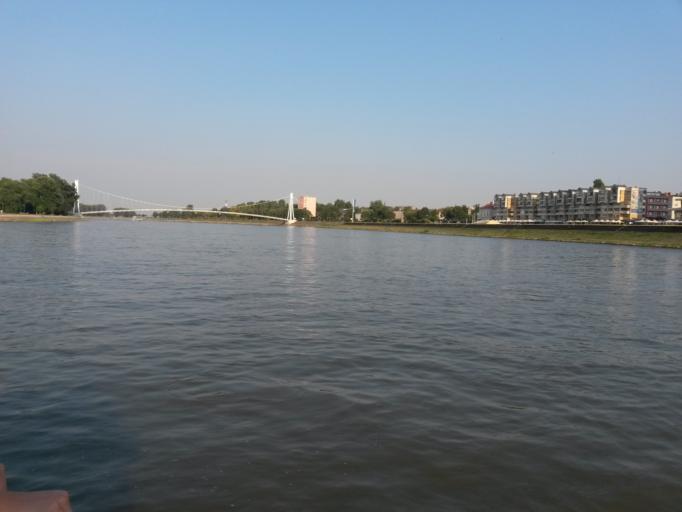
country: HR
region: Osjecko-Baranjska
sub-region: Grad Osijek
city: Osijek
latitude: 45.5644
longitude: 18.6780
